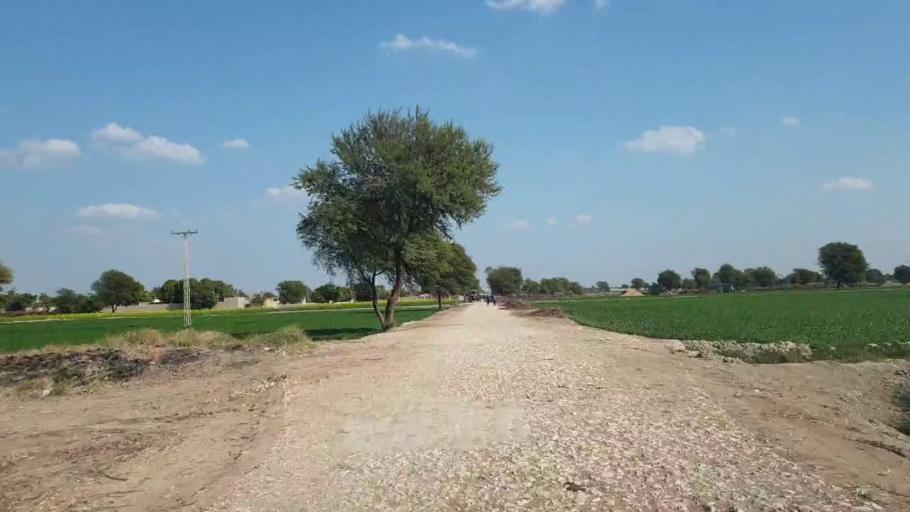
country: PK
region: Sindh
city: Shahpur Chakar
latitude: 26.1023
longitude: 68.5723
